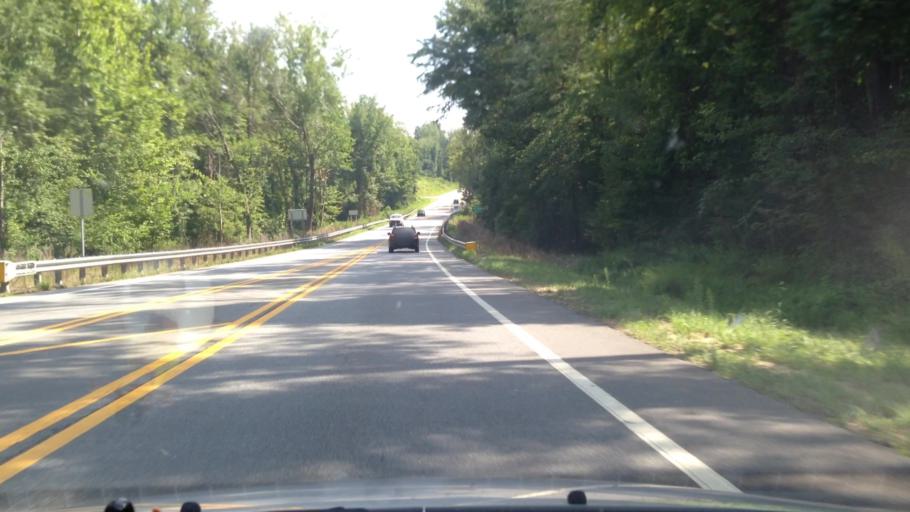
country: US
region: North Carolina
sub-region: Guilford County
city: Oak Ridge
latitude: 36.1998
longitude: -79.9856
